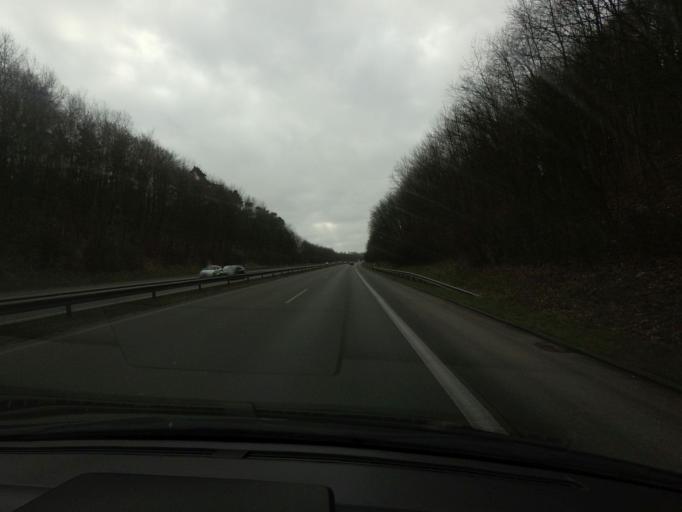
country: DE
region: Lower Saxony
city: Seevetal
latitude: 53.4144
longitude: 9.9223
